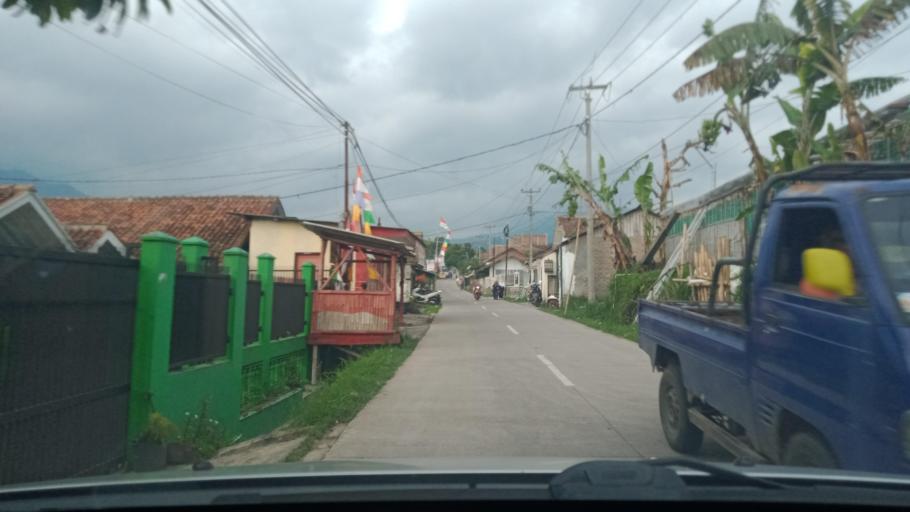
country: ID
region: West Java
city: Lembang
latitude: -6.8121
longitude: 107.5767
